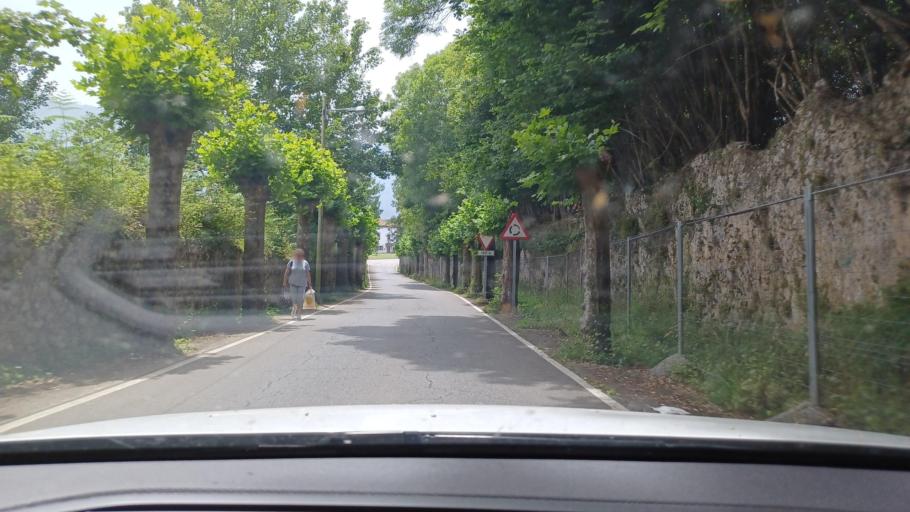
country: ES
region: Asturias
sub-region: Province of Asturias
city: Llanes
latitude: 43.4167
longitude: -4.7565
